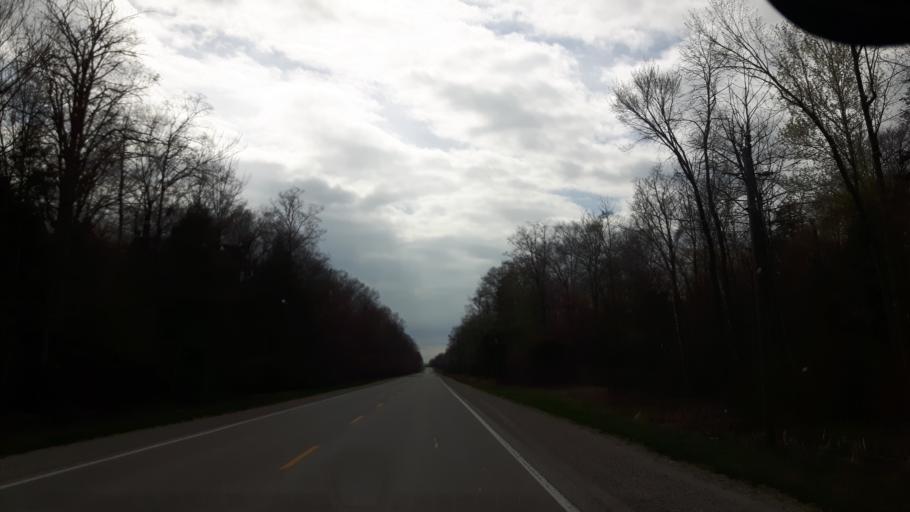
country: CA
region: Ontario
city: Bluewater
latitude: 43.5871
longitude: -81.6719
